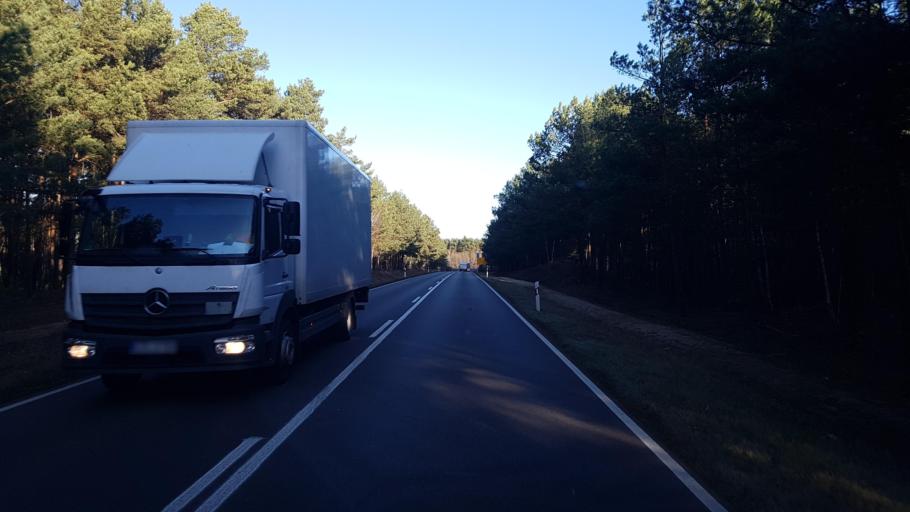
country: DE
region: Brandenburg
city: Heinersbruck
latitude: 51.7250
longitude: 14.4587
